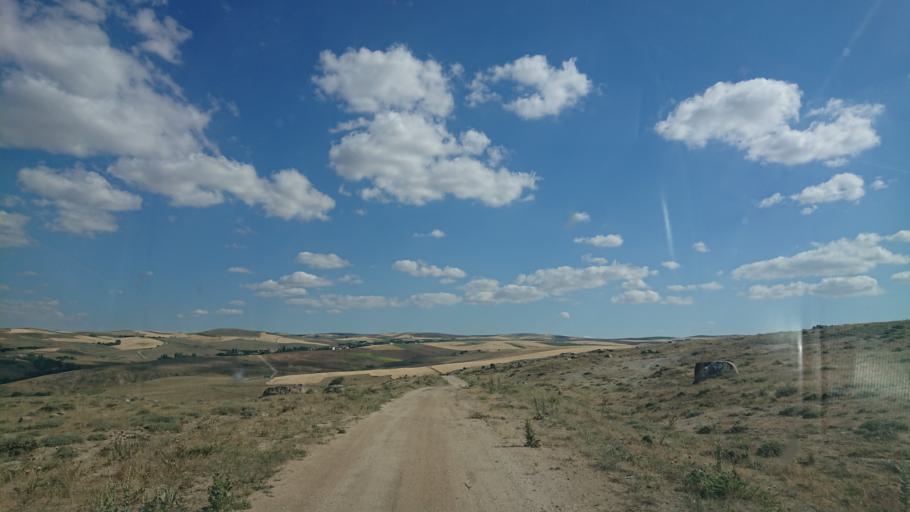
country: TR
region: Aksaray
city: Sariyahsi
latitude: 38.9245
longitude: 33.8525
